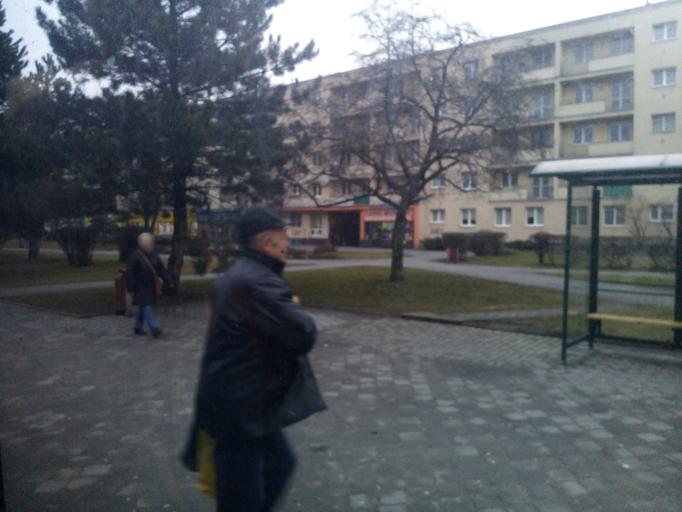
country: PL
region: Lesser Poland Voivodeship
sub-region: Powiat nowosadecki
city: Nowy Sacz
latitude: 49.6087
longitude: 20.7009
